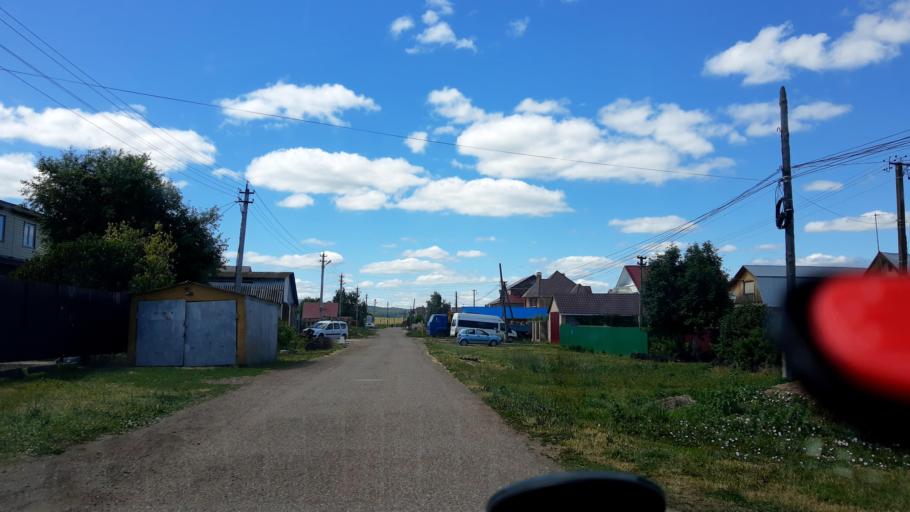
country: RU
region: Bashkortostan
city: Mikhaylovka
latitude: 54.8175
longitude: 55.7944
